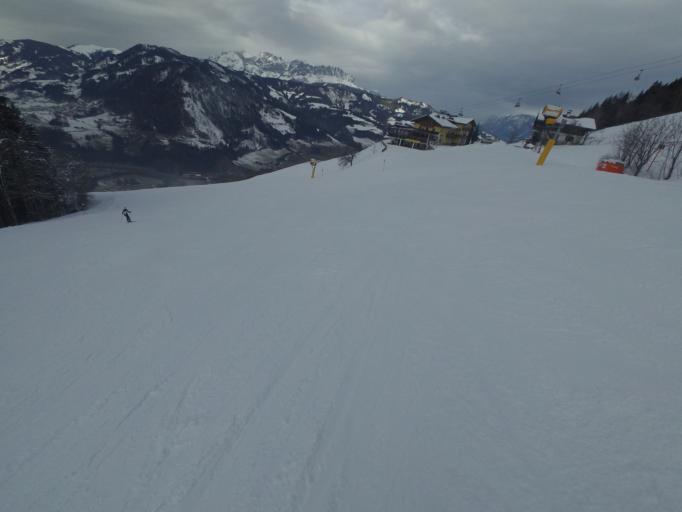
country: AT
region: Salzburg
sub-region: Politischer Bezirk Sankt Johann im Pongau
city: Sankt Johann im Pongau
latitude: 47.3194
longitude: 13.2054
